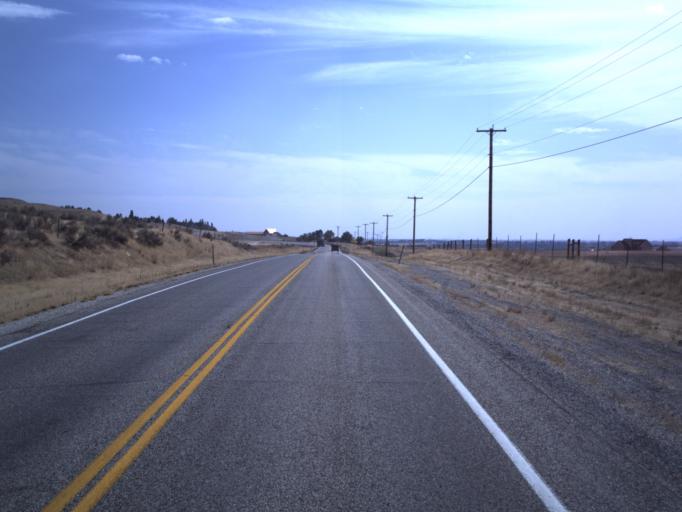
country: US
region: Utah
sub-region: Box Elder County
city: Garland
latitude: 41.7497
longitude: -112.0991
